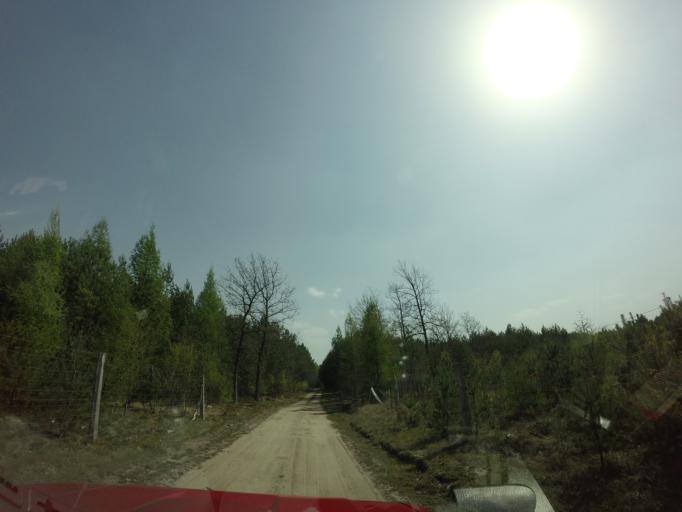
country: PL
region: West Pomeranian Voivodeship
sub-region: Powiat choszczenski
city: Drawno
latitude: 53.2342
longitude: 15.6879
